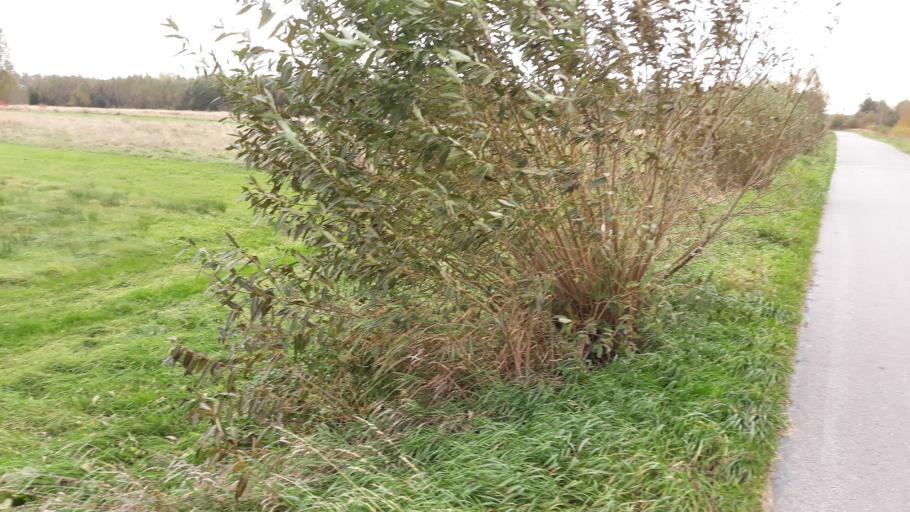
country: PL
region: Lublin Voivodeship
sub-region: Powiat janowski
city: Dzwola
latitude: 50.6706
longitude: 22.5808
